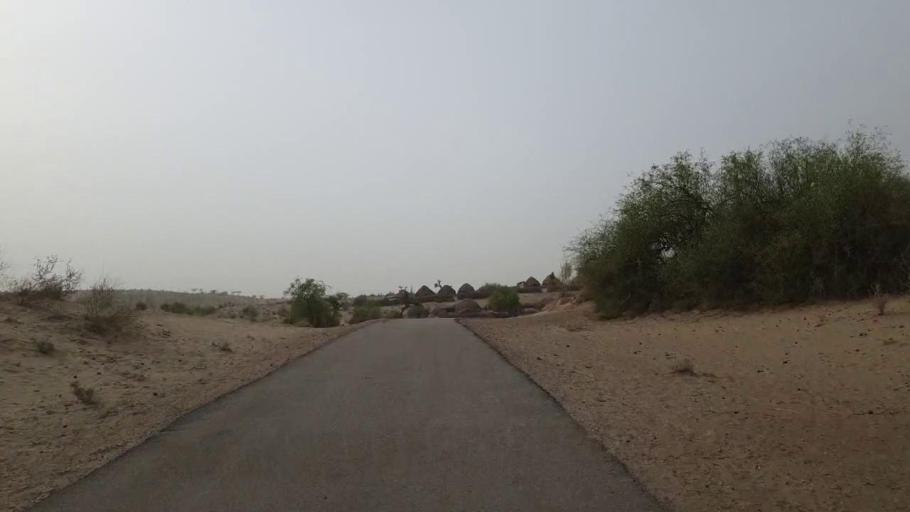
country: PK
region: Sindh
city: Islamkot
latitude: 24.5774
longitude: 70.3651
